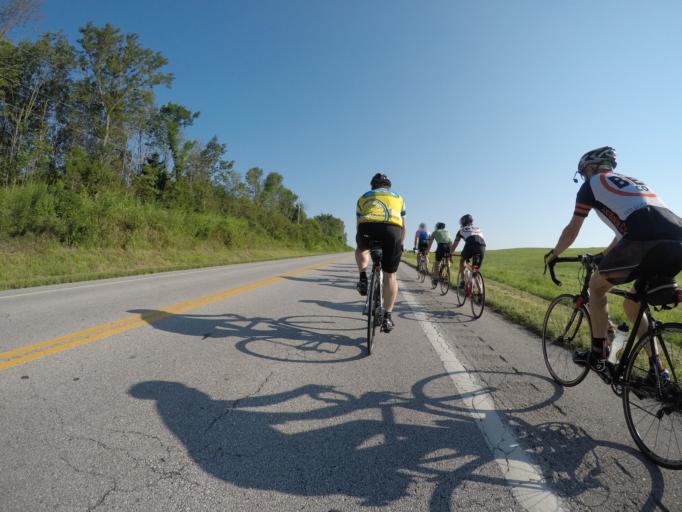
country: US
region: Missouri
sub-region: Platte County
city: Weston
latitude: 39.3895
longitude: -94.8640
